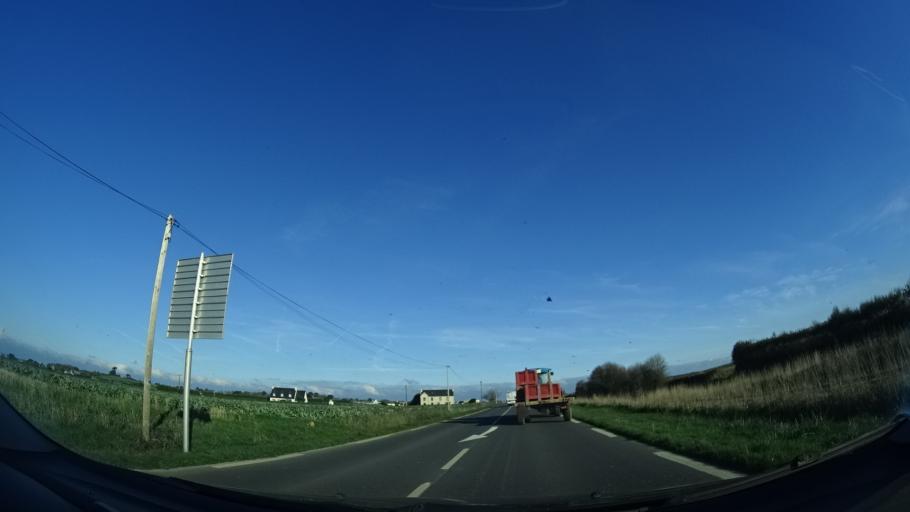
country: FR
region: Brittany
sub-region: Departement du Finistere
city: Saint-Pol-de-Leon
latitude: 48.6969
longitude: -3.9958
